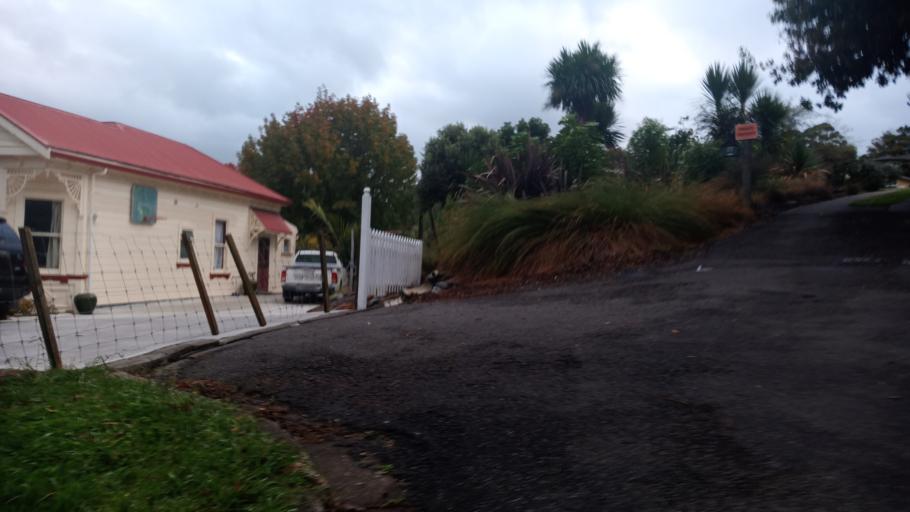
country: NZ
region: Gisborne
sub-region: Gisborne District
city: Gisborne
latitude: -38.6420
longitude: 178.0148
